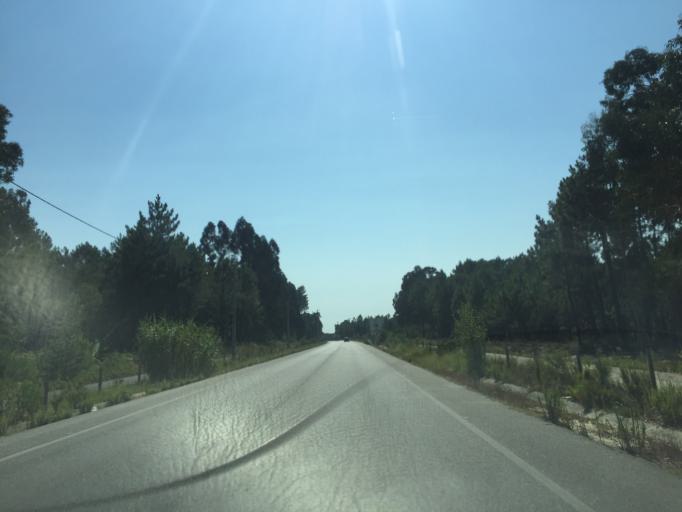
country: PT
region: Coimbra
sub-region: Montemor-O-Velho
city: Arazede
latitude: 40.3281
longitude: -8.6642
